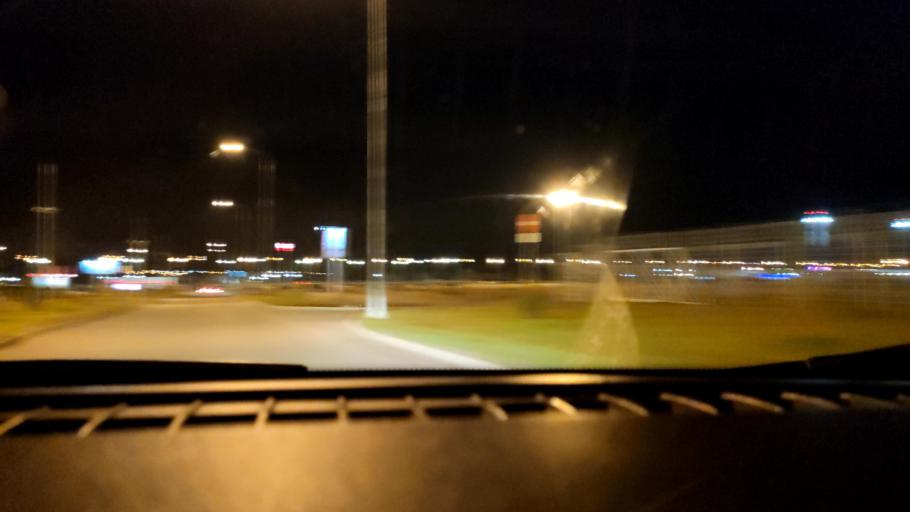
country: RU
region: Perm
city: Kultayevo
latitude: 57.9174
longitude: 56.0104
